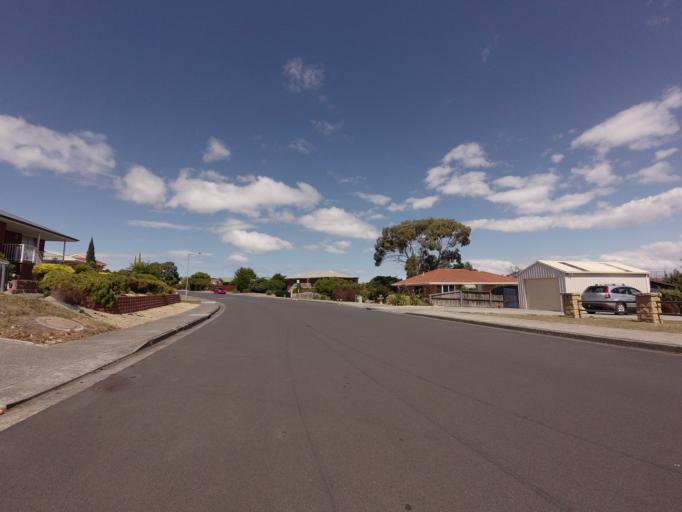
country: AU
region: Tasmania
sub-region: Clarence
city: Rokeby
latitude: -42.8994
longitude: 147.4566
